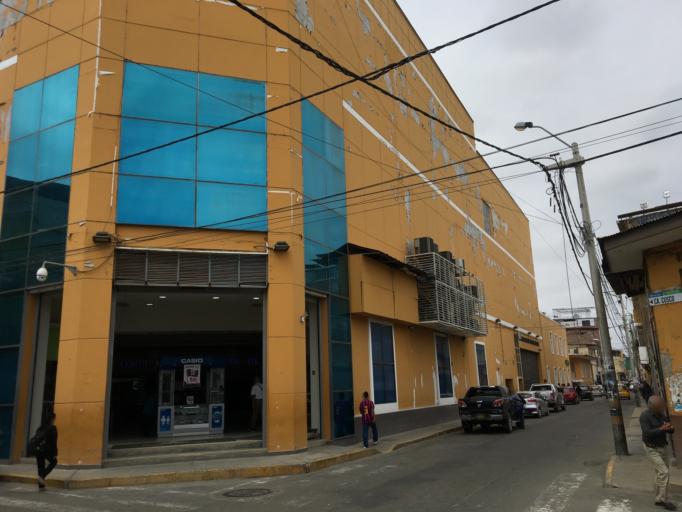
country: PE
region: Piura
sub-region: Provincia de Piura
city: Piura
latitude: -5.1964
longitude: -80.6286
